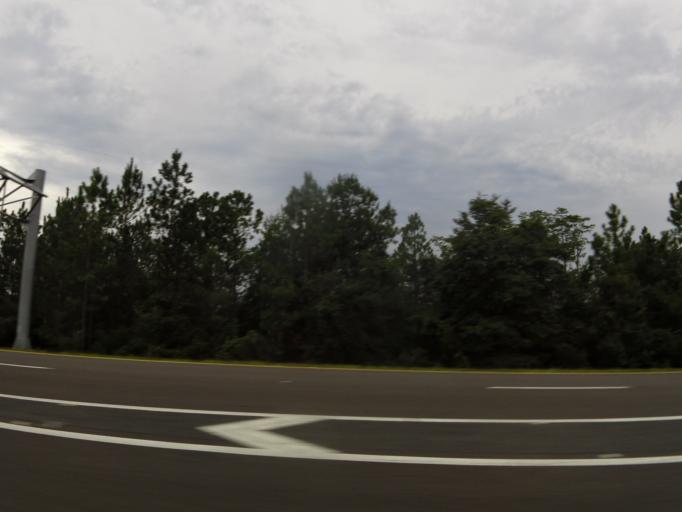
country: US
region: Florida
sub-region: Duval County
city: Baldwin
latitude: 30.2988
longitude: -81.8783
